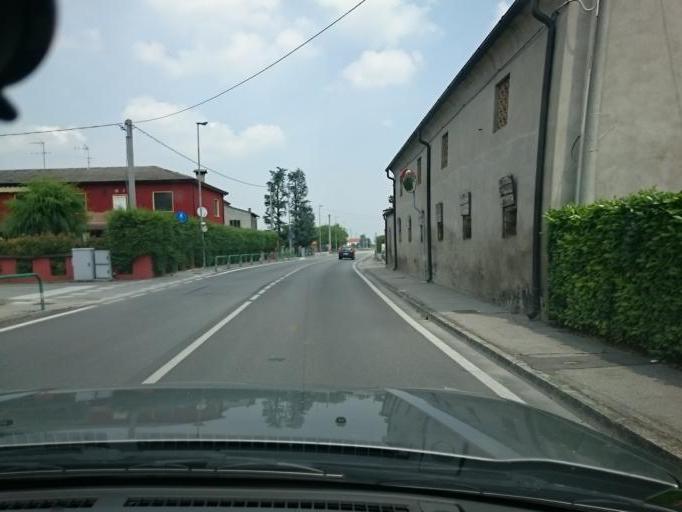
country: IT
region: Veneto
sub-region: Provincia di Padova
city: Brugine
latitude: 45.3010
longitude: 11.9925
